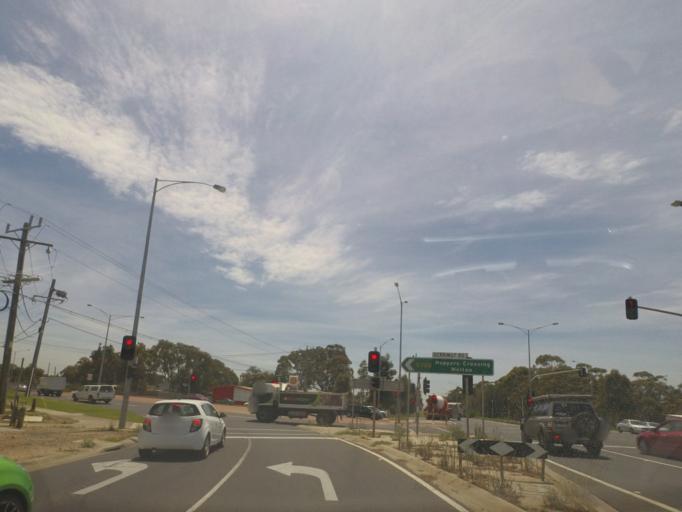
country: AU
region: Victoria
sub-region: Wyndham
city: Werribee
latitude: -37.8939
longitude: 144.6801
